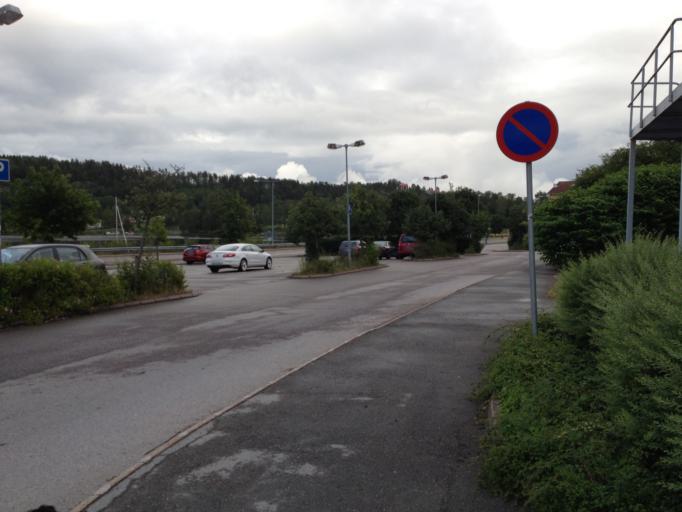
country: SE
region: Vaestra Goetaland
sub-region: Bengtsfors Kommun
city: Bengtsfors
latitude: 59.0311
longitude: 12.2216
